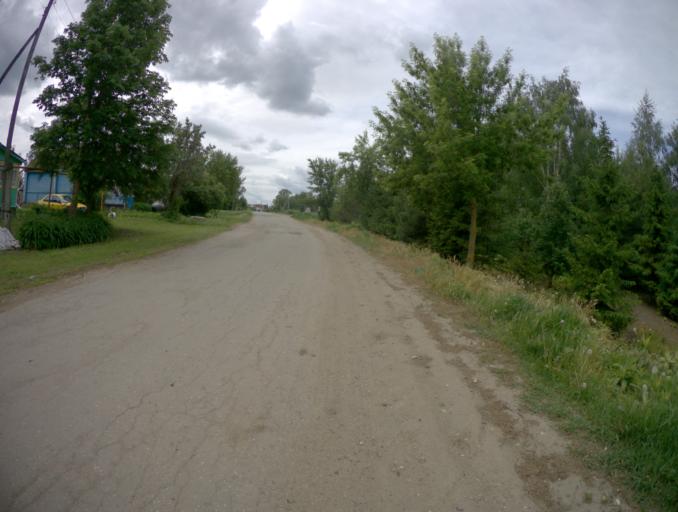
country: RU
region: Vladimir
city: Stavrovo
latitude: 56.2360
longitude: 39.8898
